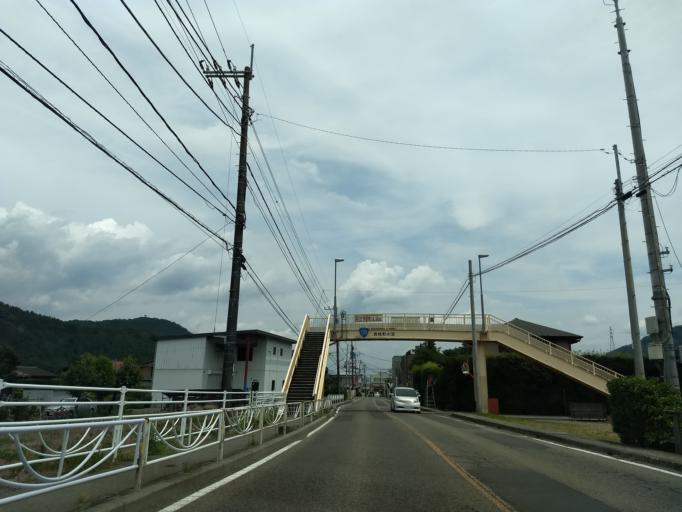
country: JP
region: Yamanashi
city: Otsuki
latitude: 35.5219
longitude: 138.8428
